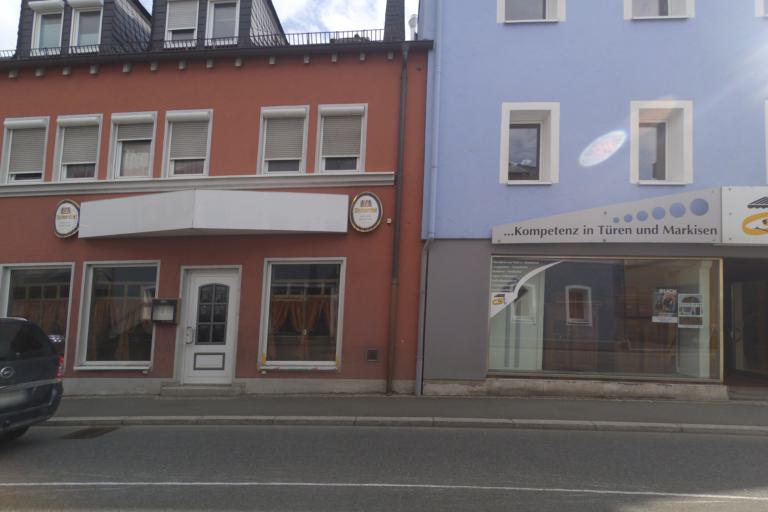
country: DE
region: Bavaria
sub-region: Upper Franconia
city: Munchberg
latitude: 50.1912
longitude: 11.7870
